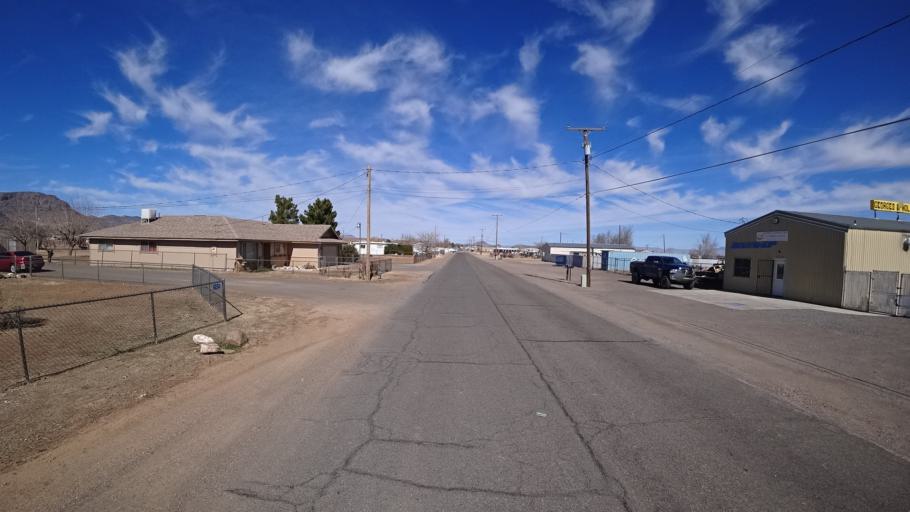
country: US
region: Arizona
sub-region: Mohave County
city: New Kingman-Butler
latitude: 35.2448
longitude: -114.0132
